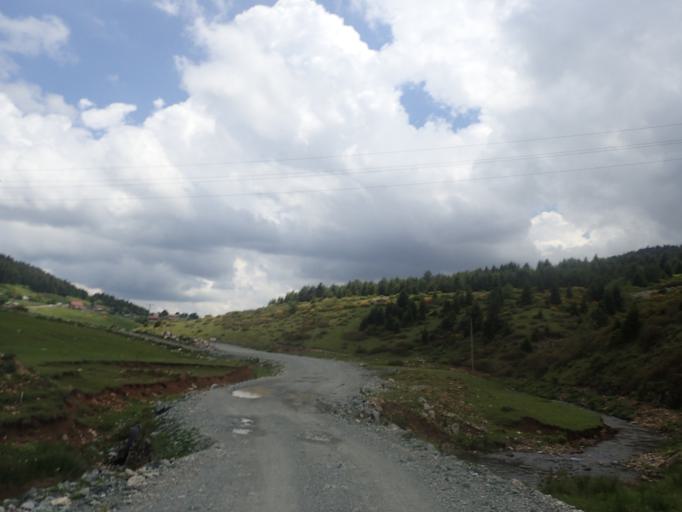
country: TR
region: Ordu
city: Topcam
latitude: 40.6838
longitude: 37.9412
